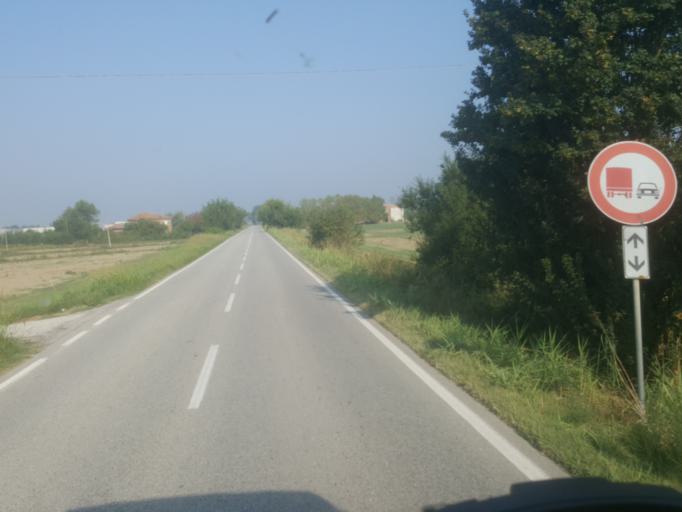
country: IT
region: Emilia-Romagna
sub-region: Provincia di Ravenna
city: Lavezzola
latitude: 44.5686
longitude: 11.8922
